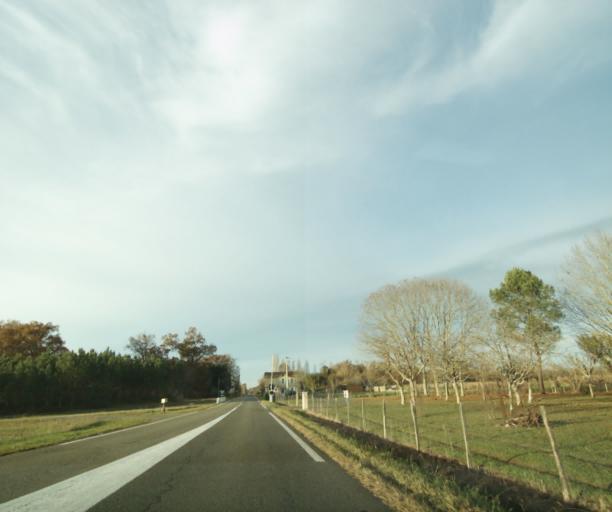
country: FR
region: Aquitaine
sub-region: Departement des Landes
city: Gabarret
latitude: 43.9902
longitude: -0.0071
